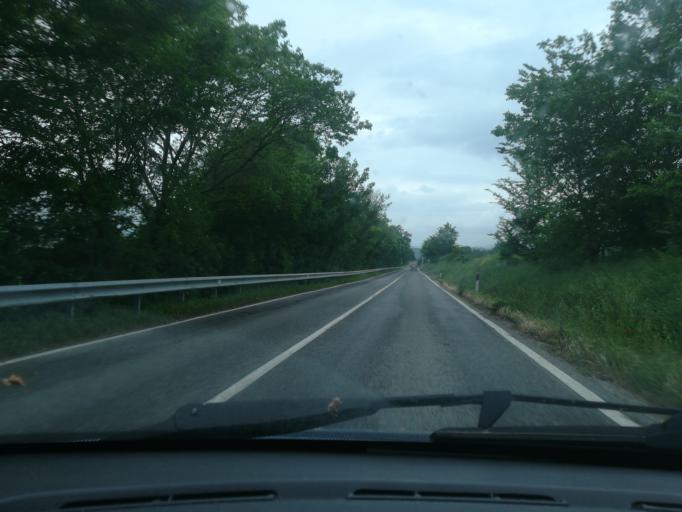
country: IT
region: The Marches
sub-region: Provincia di Macerata
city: Treia
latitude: 43.2693
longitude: 13.2687
